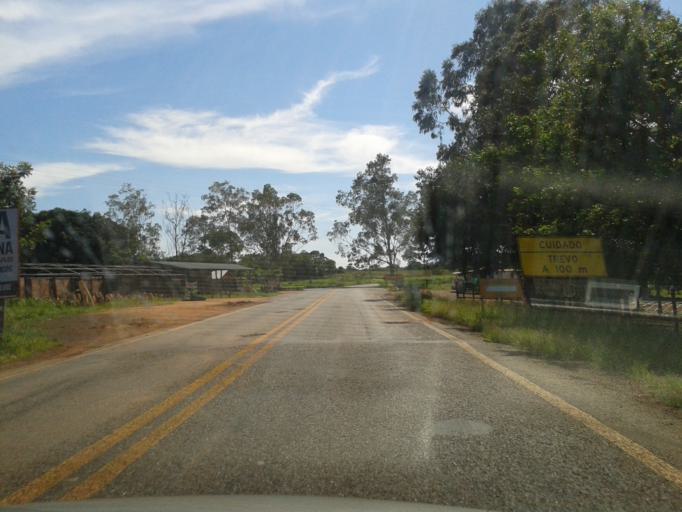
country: BR
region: Goias
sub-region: Piracanjuba
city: Piracanjuba
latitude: -17.2314
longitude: -48.7132
